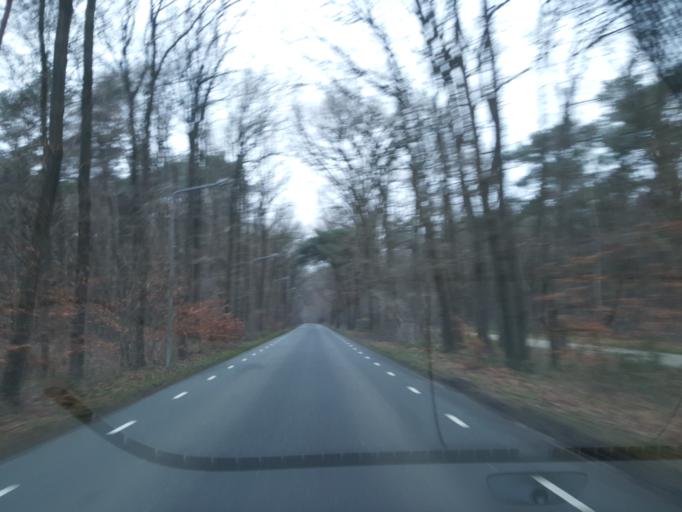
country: NL
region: North Holland
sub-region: Gemeente Wijdemeren
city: Nieuw-Loosdrecht
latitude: 52.1847
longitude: 5.1741
